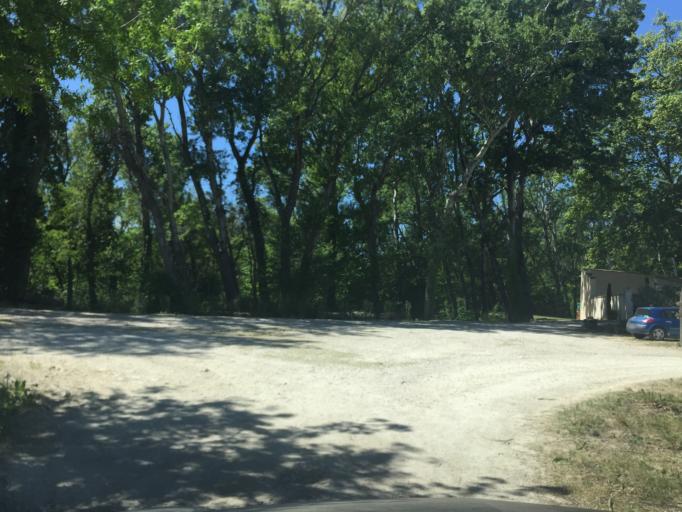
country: FR
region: Languedoc-Roussillon
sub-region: Departement du Gard
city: Roquemaure
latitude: 44.0528
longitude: 4.7982
